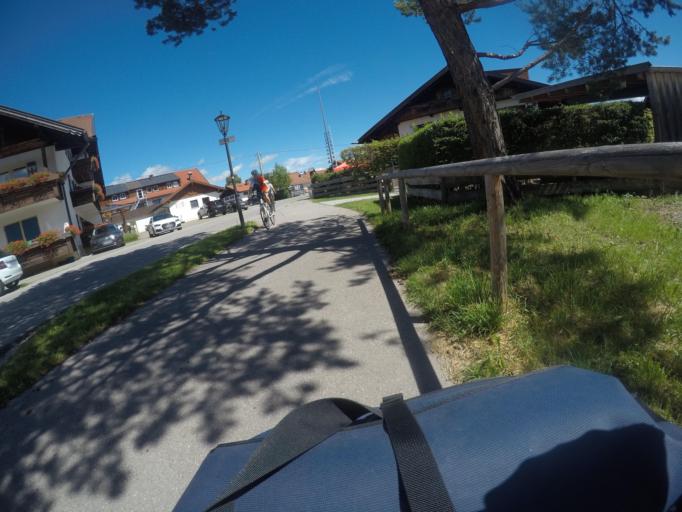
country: DE
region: Bavaria
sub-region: Swabia
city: Schwangau
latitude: 47.5758
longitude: 10.7368
